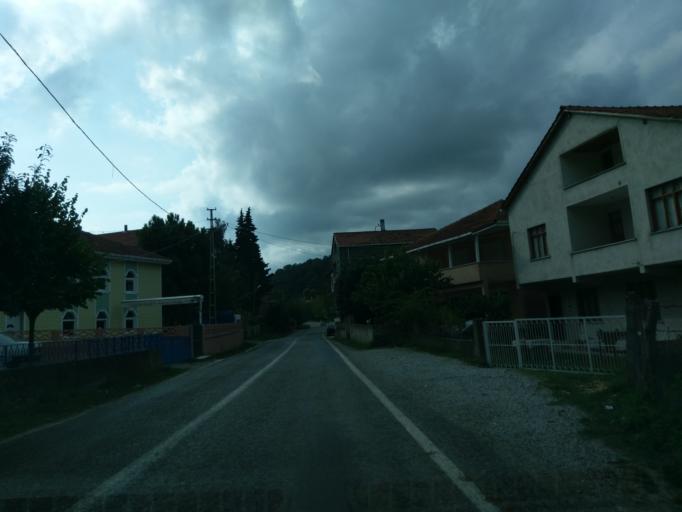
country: TR
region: Sinop
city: Helaldi
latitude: 41.9362
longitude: 34.4089
